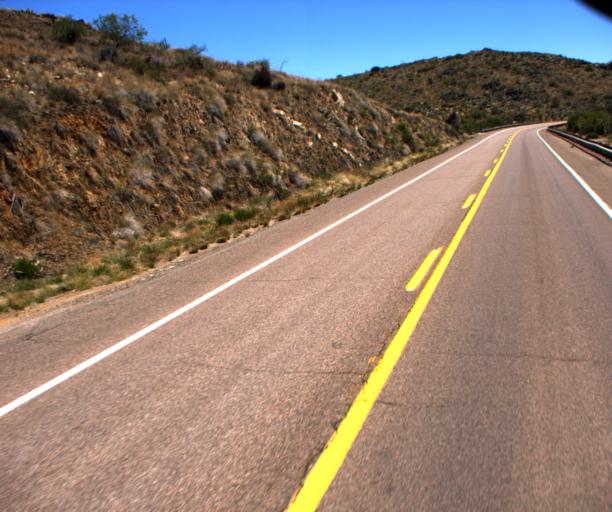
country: US
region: Arizona
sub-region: Yavapai County
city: Bagdad
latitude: 34.5565
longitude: -113.1578
